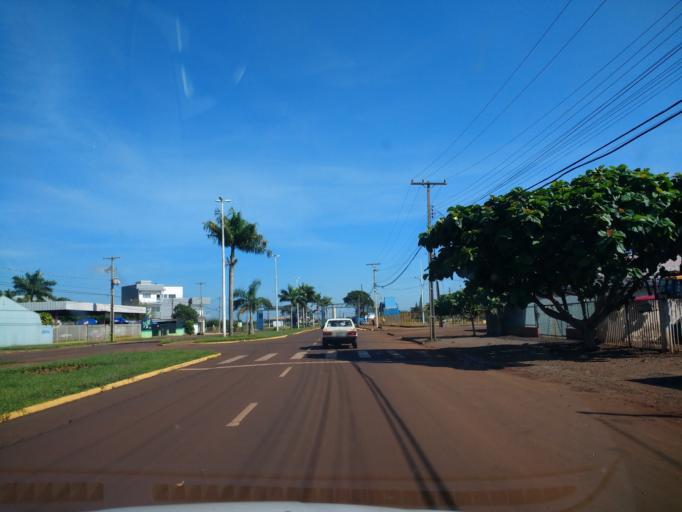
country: BR
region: Parana
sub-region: Palotina
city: Palotina
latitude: -24.4092
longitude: -53.5313
